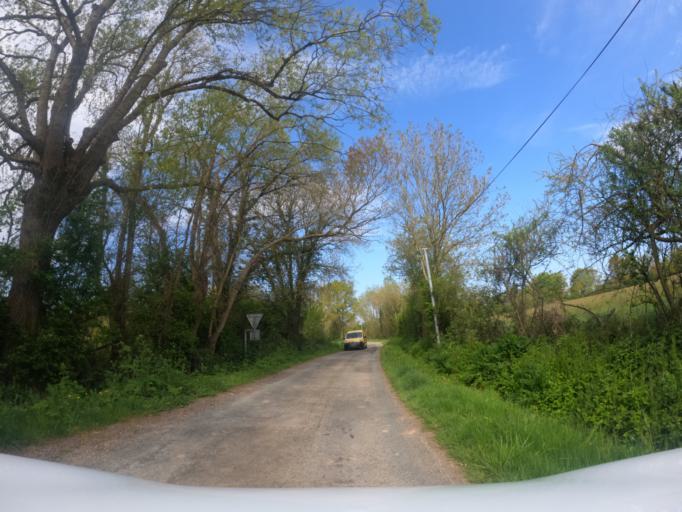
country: FR
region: Pays de la Loire
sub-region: Departement de la Vendee
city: Le Champ-Saint-Pere
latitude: 46.5201
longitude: -1.3366
